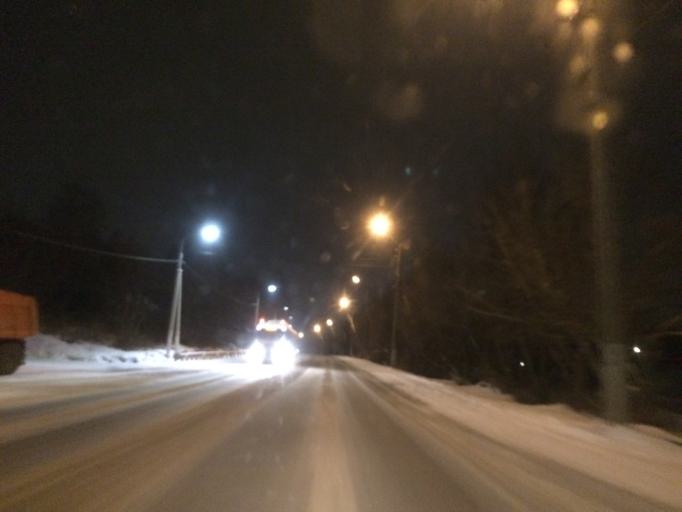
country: RU
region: Tula
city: Tula
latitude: 54.2234
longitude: 37.6520
